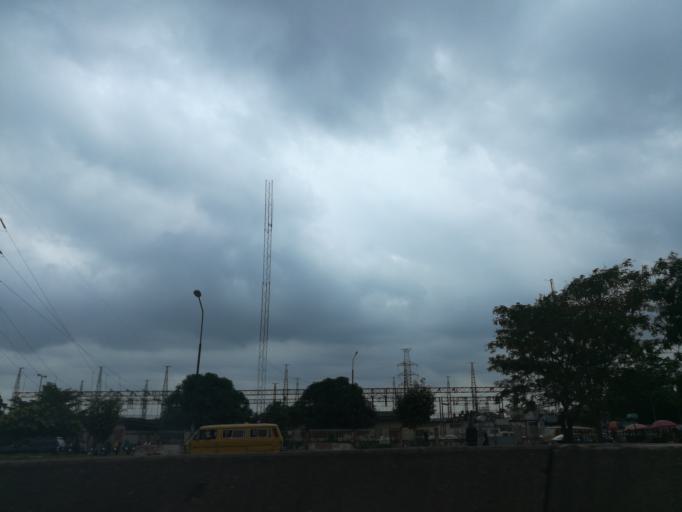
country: NG
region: Lagos
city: Somolu
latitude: 6.5492
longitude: 3.3892
